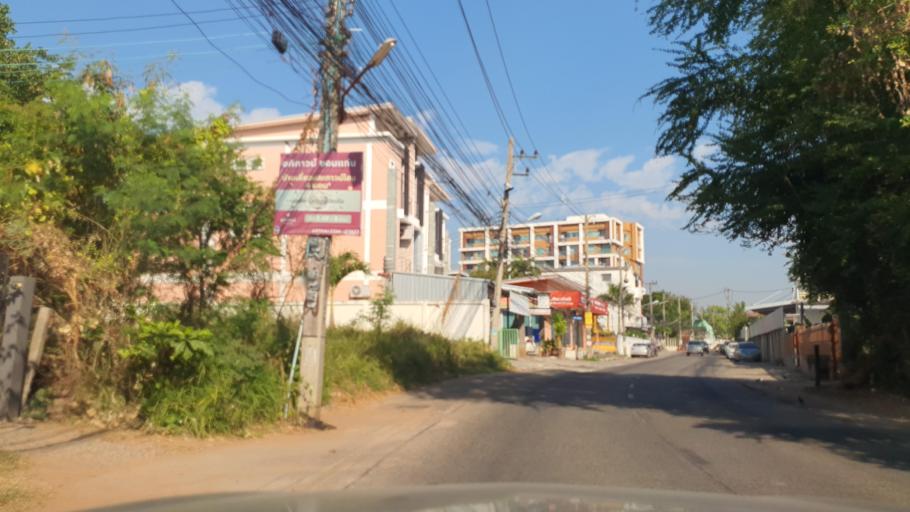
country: TH
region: Khon Kaen
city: Khon Kaen
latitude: 16.4388
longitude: 102.8136
